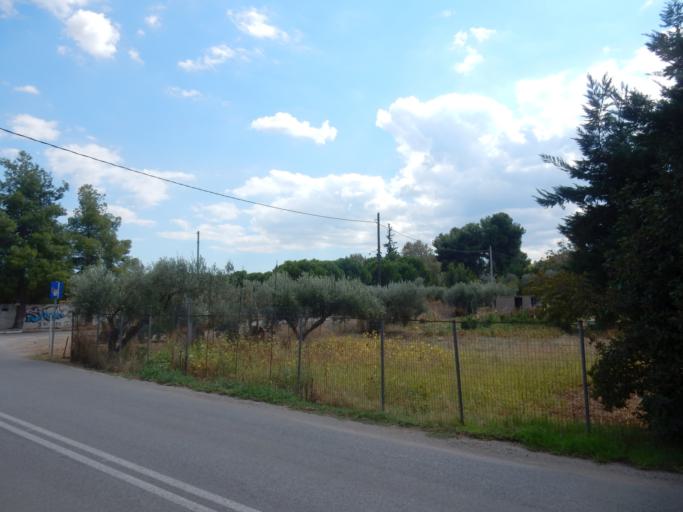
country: GR
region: Attica
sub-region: Nomarchia Anatolikis Attikis
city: Khalkoutsion
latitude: 38.3305
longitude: 23.7369
